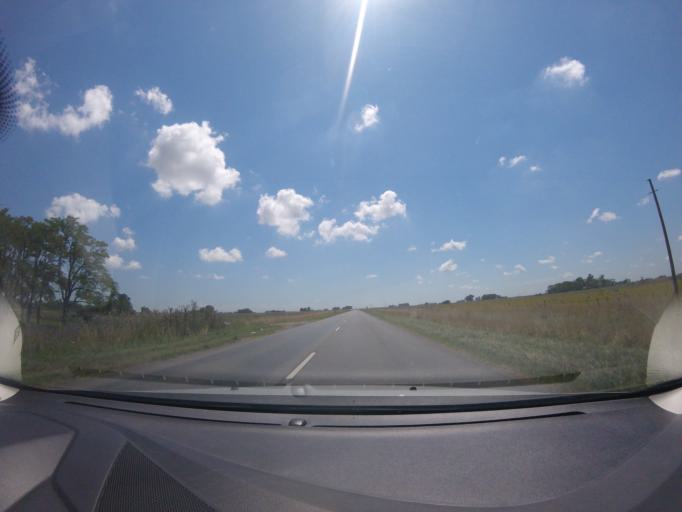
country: AR
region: Buenos Aires
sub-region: Partido de Rauch
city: Rauch
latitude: -36.7435
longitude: -59.0648
